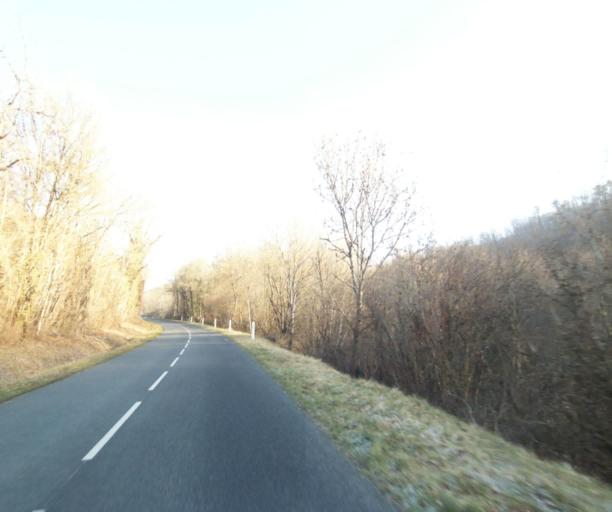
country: FR
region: Champagne-Ardenne
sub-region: Departement de la Haute-Marne
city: Chevillon
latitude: 48.5253
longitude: 5.1612
